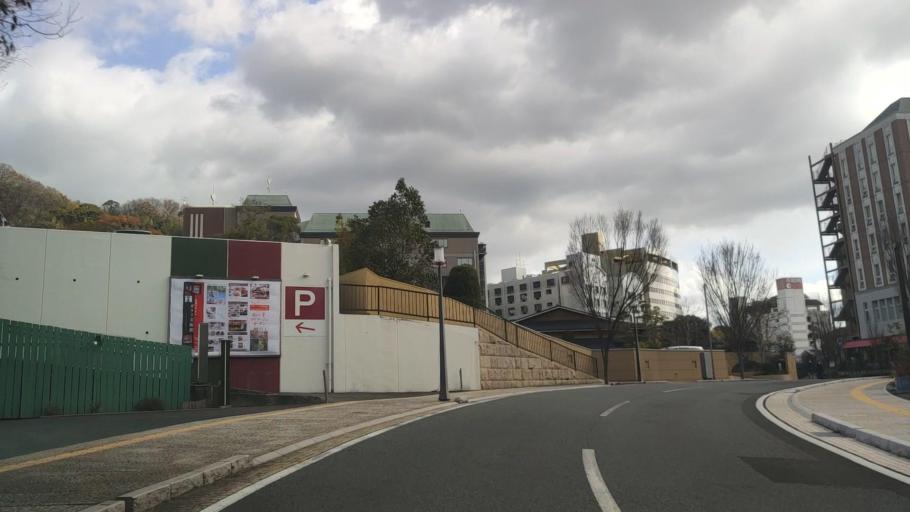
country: JP
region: Ehime
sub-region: Shikoku-chuo Shi
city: Matsuyama
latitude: 33.8541
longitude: 132.7853
